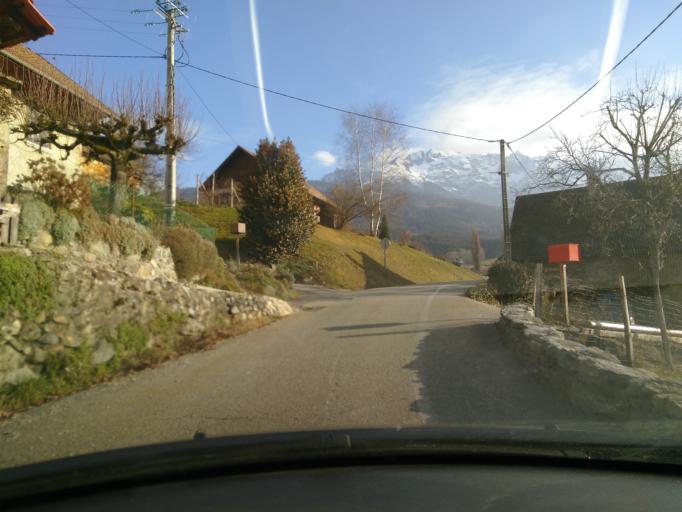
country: FR
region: Rhone-Alpes
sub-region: Departement de l'Isere
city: Villard-Bonnot
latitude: 45.2346
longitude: 5.9271
